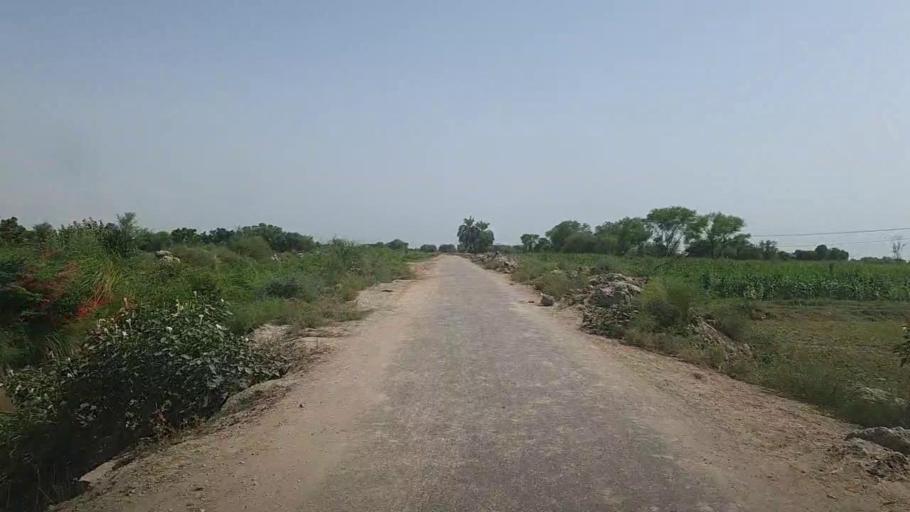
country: PK
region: Sindh
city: Pad Idan
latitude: 26.8170
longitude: 68.3277
